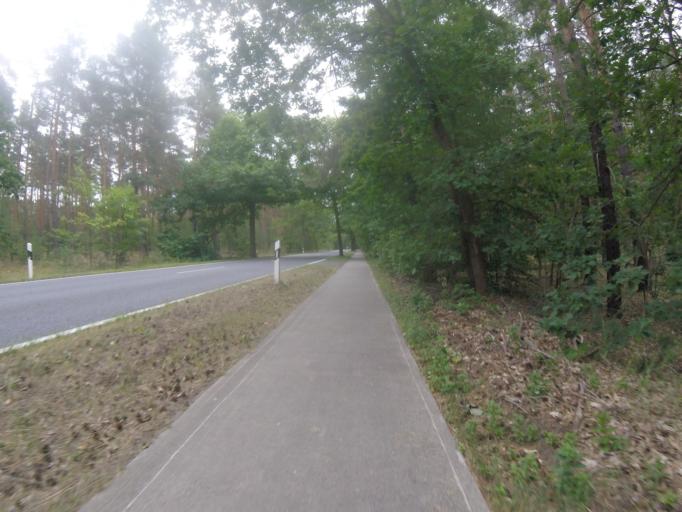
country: DE
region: Brandenburg
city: Bestensee
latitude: 52.2582
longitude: 13.6326
